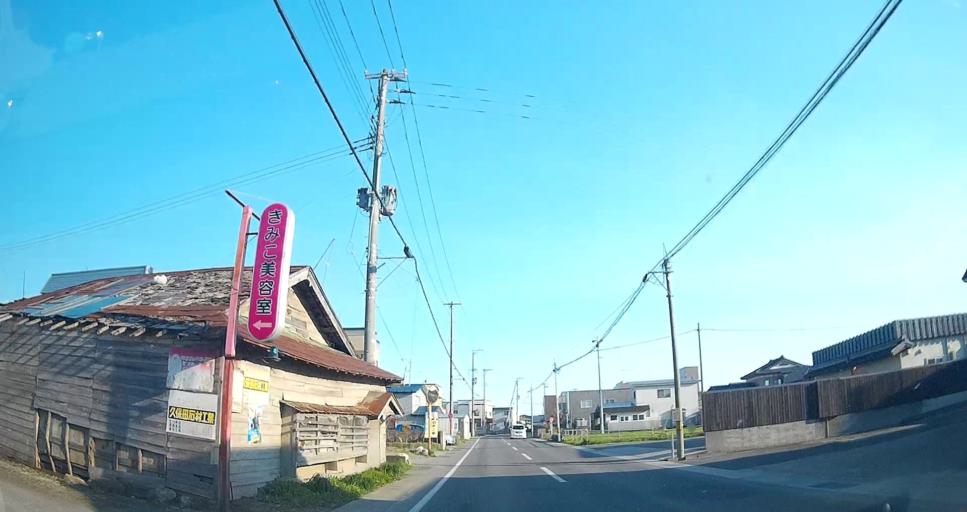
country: JP
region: Aomori
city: Mutsu
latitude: 41.2878
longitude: 141.2115
